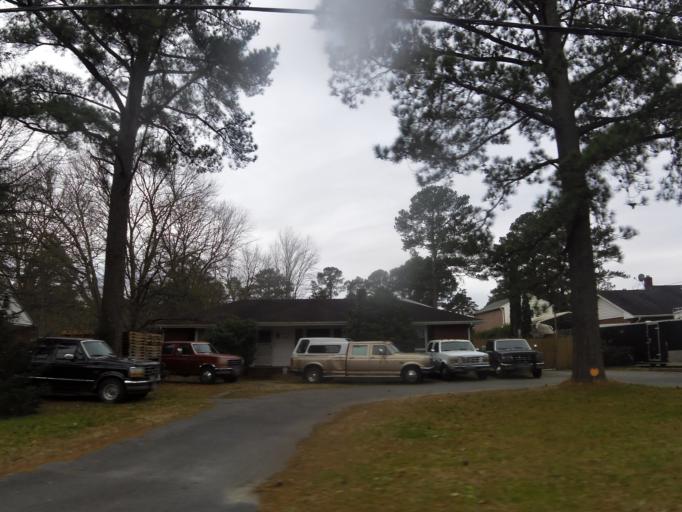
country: US
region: Virginia
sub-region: City of Portsmouth
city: Portsmouth Heights
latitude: 36.8549
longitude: -76.3835
